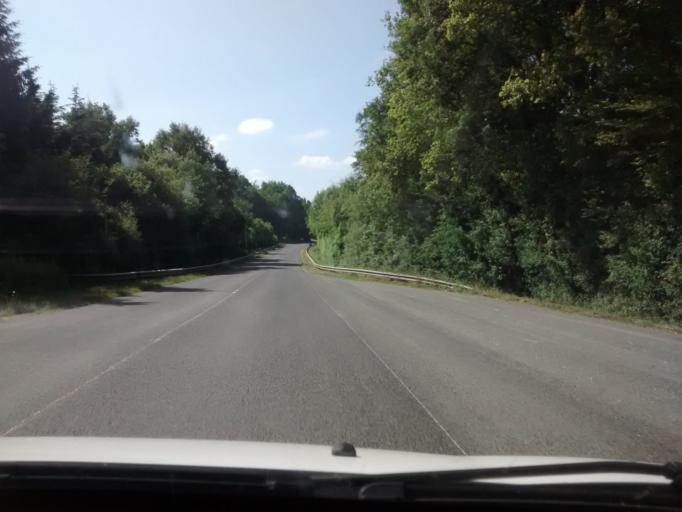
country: FR
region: Pays de la Loire
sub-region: Departement de la Sarthe
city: Vibraye
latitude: 48.0002
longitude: 0.7618
